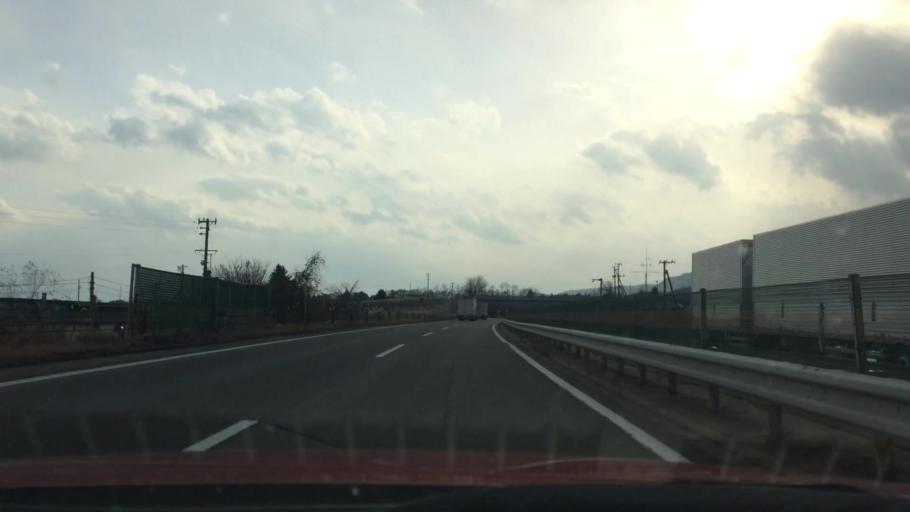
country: JP
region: Nagano
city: Ina
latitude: 35.6793
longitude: 137.9084
